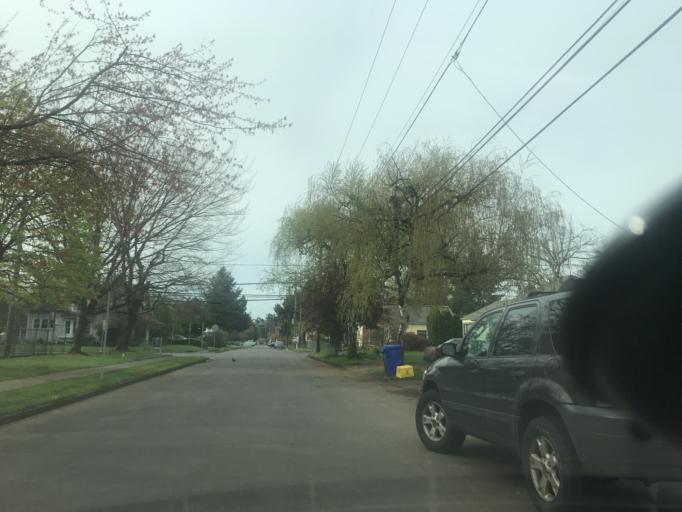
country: US
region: Oregon
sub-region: Multnomah County
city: Lents
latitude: 45.4946
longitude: -122.5847
